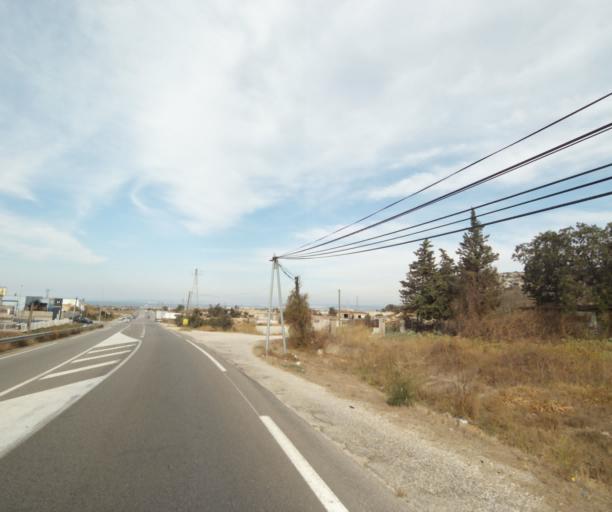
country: FR
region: Provence-Alpes-Cote d'Azur
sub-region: Departement des Bouches-du-Rhone
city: Gignac-la-Nerthe
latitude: 43.3758
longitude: 5.2276
